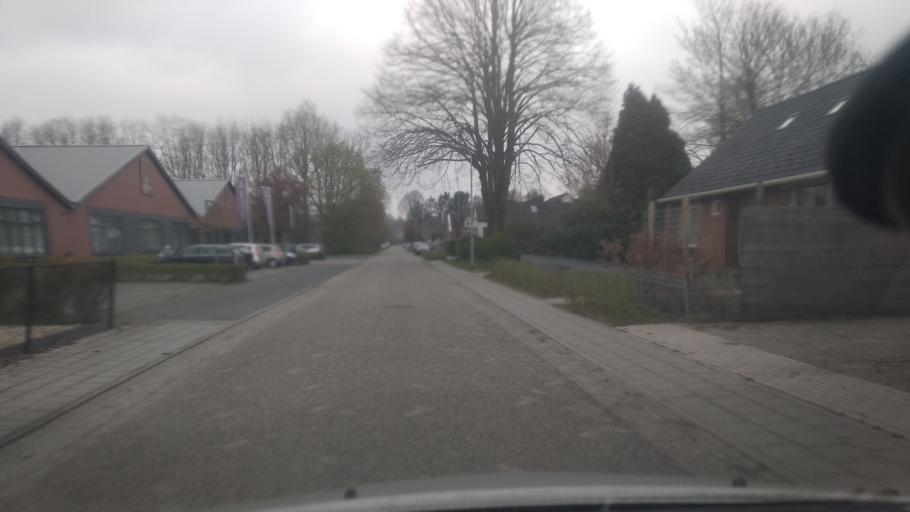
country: NL
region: Groningen
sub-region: Gemeente Stadskanaal
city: Stadskanaal
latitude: 52.9650
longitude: 6.9688
